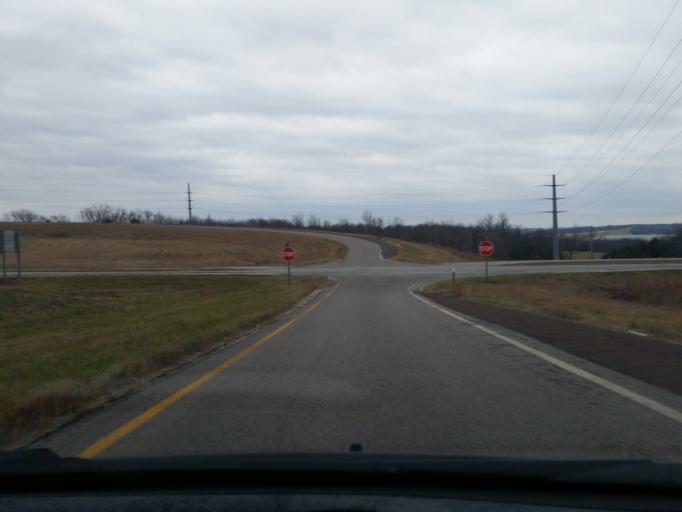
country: US
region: Kansas
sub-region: Douglas County
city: Lawrence
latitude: 38.9439
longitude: -95.3370
